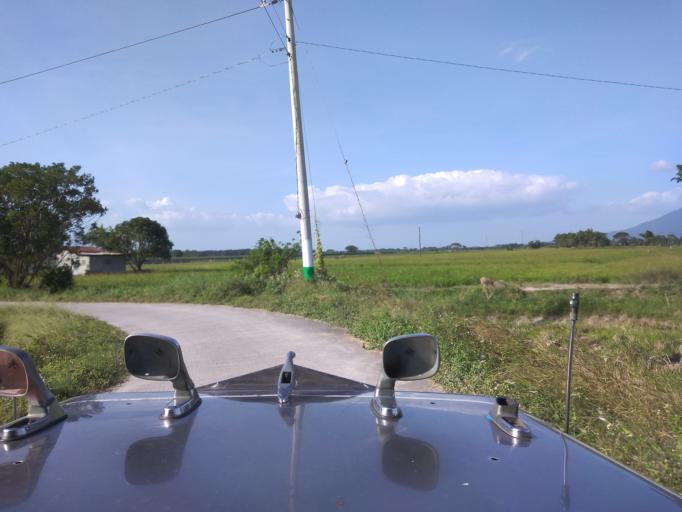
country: PH
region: Central Luzon
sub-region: Province of Pampanga
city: Malino
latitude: 15.1001
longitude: 120.6946
